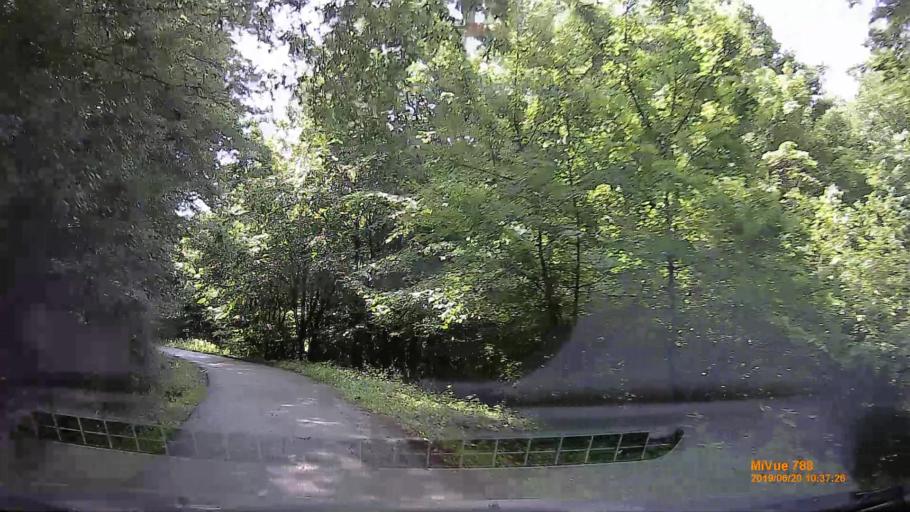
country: HU
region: Baranya
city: Hidas
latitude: 46.2043
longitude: 18.5327
